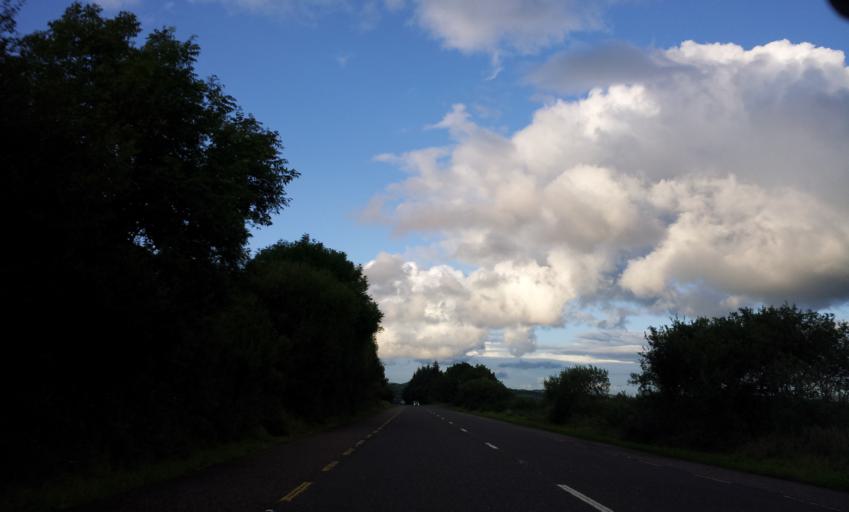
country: IE
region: Munster
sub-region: Ciarrai
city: Castleisland
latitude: 52.2946
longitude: -9.3928
